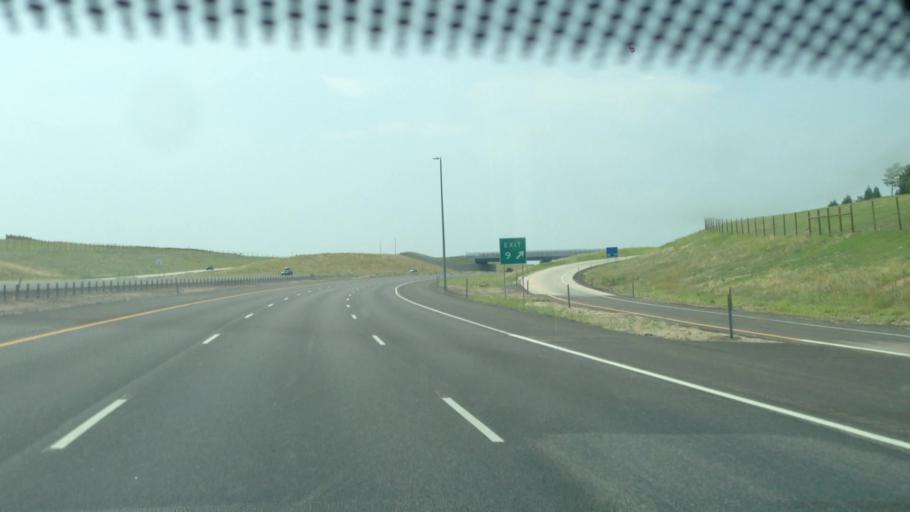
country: US
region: Colorado
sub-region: Douglas County
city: Parker
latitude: 39.5811
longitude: -104.7198
